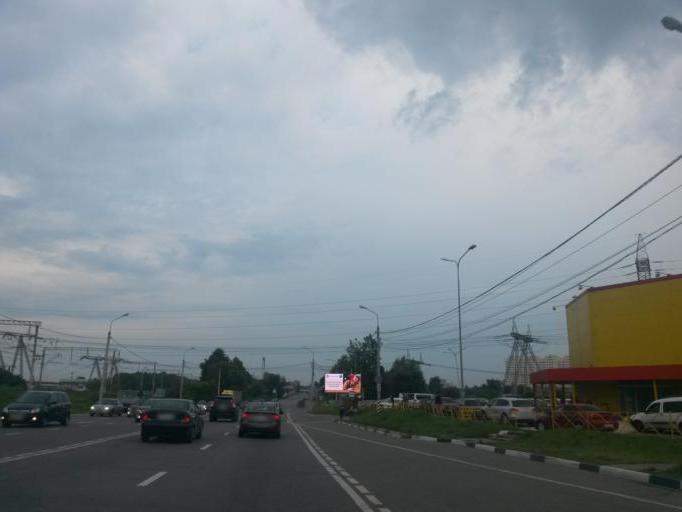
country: RU
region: Moskovskaya
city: Domodedovo
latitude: 55.4602
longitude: 37.7578
